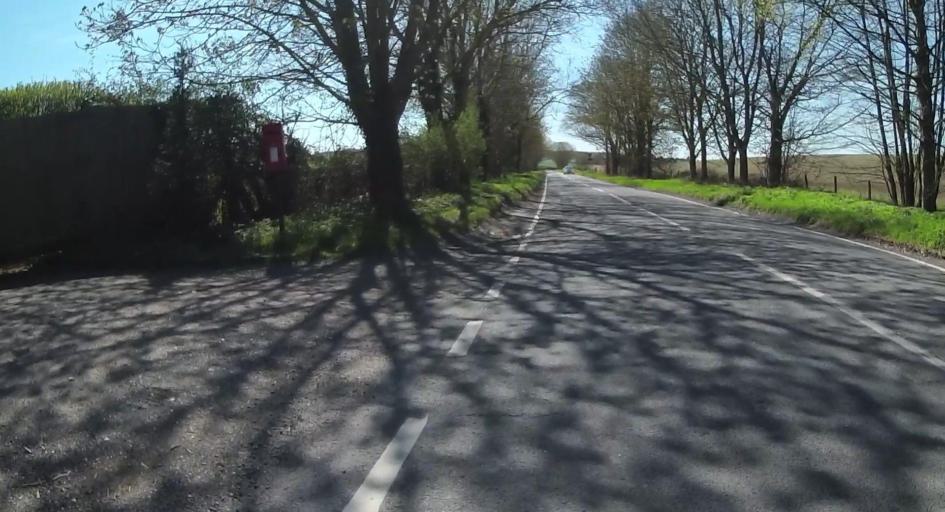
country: GB
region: England
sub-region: Hampshire
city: Winchester
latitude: 51.1001
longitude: -1.4008
